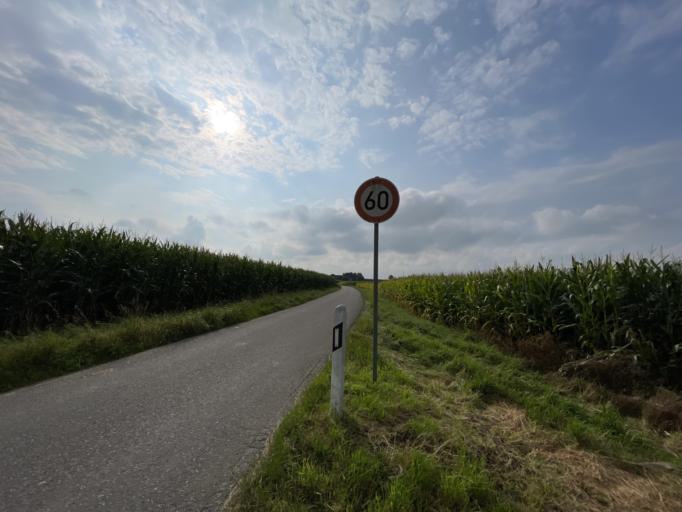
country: DE
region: Saxony
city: Claussnitz
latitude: 50.9757
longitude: 12.8642
